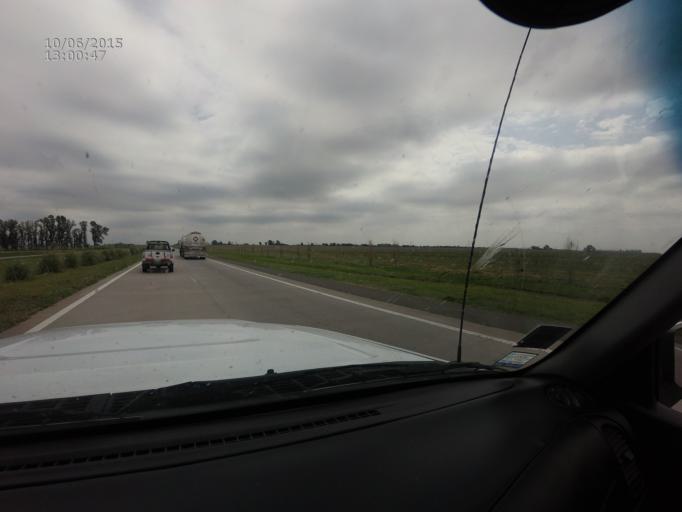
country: AR
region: Santa Fe
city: Armstrong
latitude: -32.7921
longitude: -61.7065
